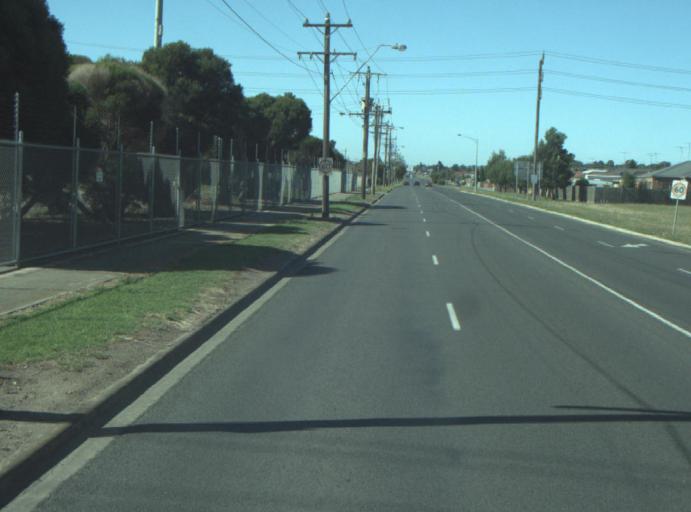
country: AU
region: Victoria
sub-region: Greater Geelong
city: Bell Post Hill
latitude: -38.0825
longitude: 144.3371
